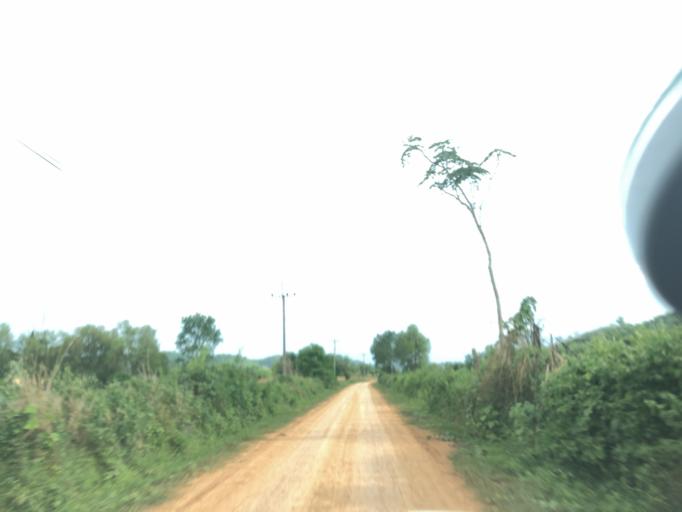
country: LA
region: Xiagnabouli
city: Muang Kenthao
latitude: 17.9933
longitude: 101.4191
